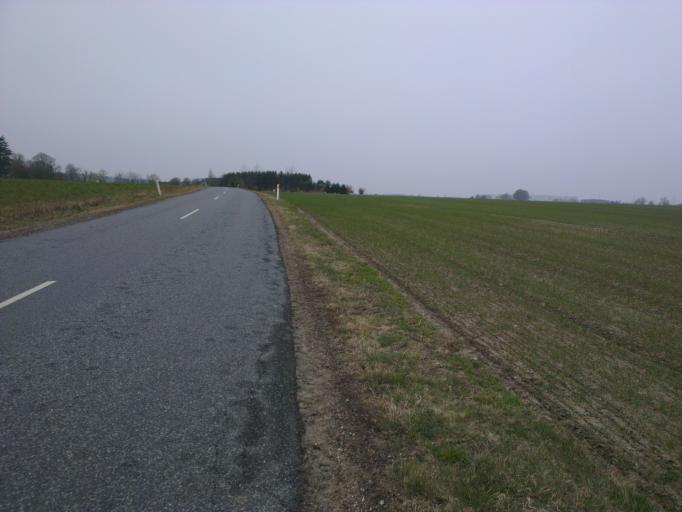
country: DK
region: Capital Region
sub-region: Frederikssund Kommune
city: Skibby
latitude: 55.7891
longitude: 11.9915
